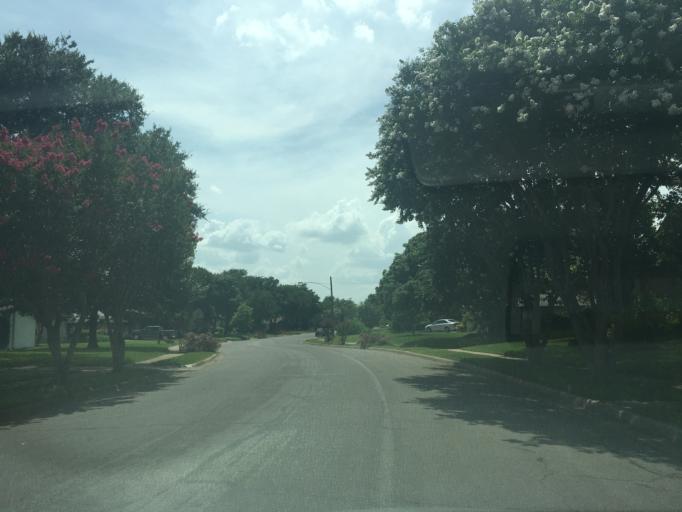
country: US
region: Texas
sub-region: Dallas County
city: Farmers Branch
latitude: 32.9131
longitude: -96.8514
